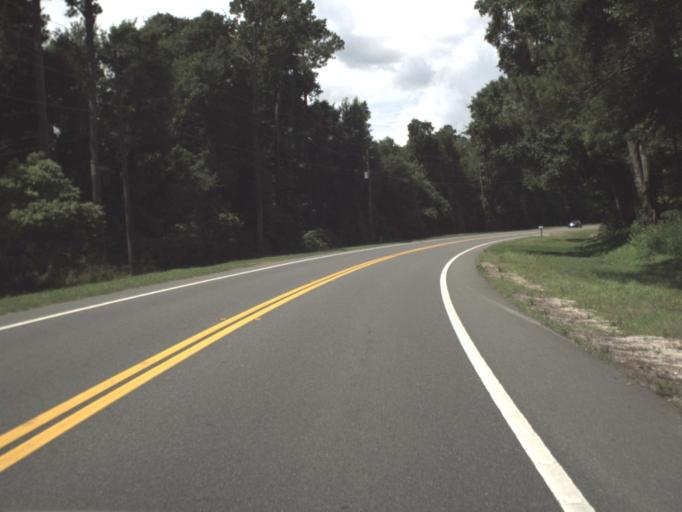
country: US
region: Florida
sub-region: Alachua County
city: Alachua
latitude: 29.8051
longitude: -82.4743
